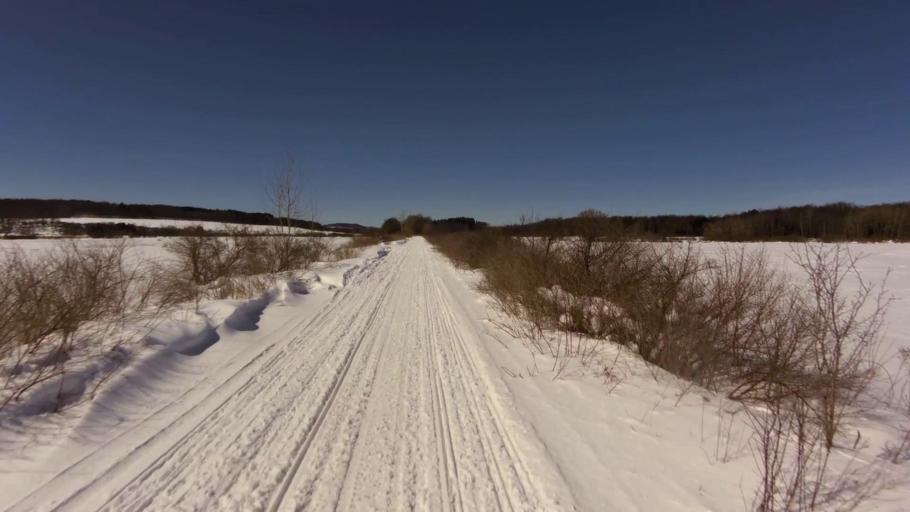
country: US
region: New York
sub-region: Cattaraugus County
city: Delevan
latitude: 42.4296
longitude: -78.3906
